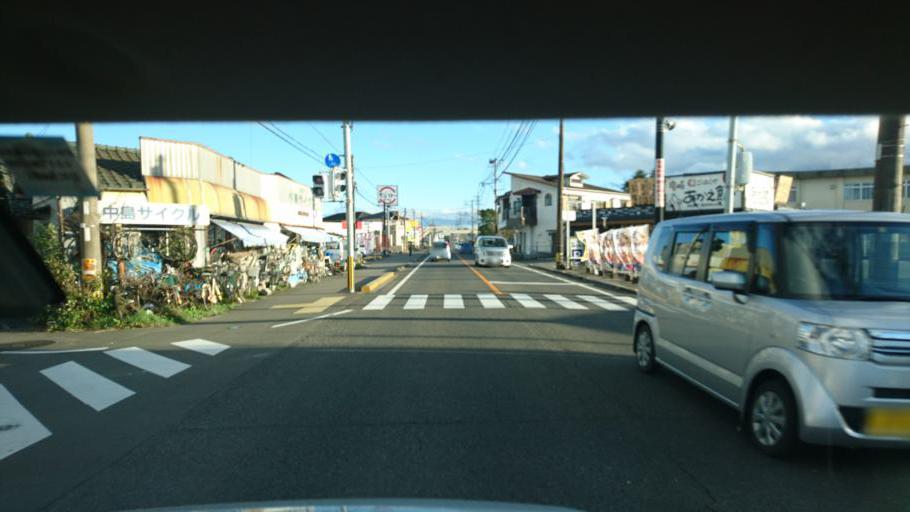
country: JP
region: Miyazaki
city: Miyazaki-shi
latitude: 31.8869
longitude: 131.4245
